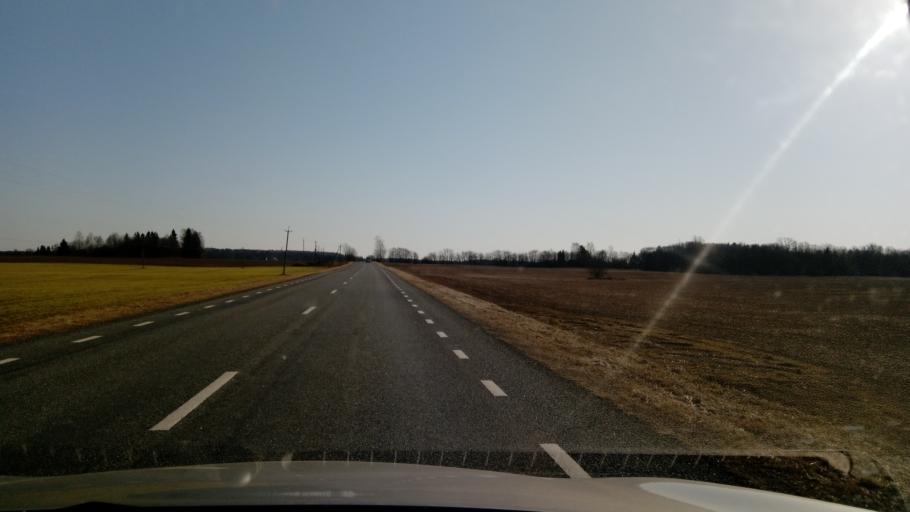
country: EE
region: Jaervamaa
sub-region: Jaerva-Jaani vald
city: Jarva-Jaani
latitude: 59.0708
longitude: 25.9402
